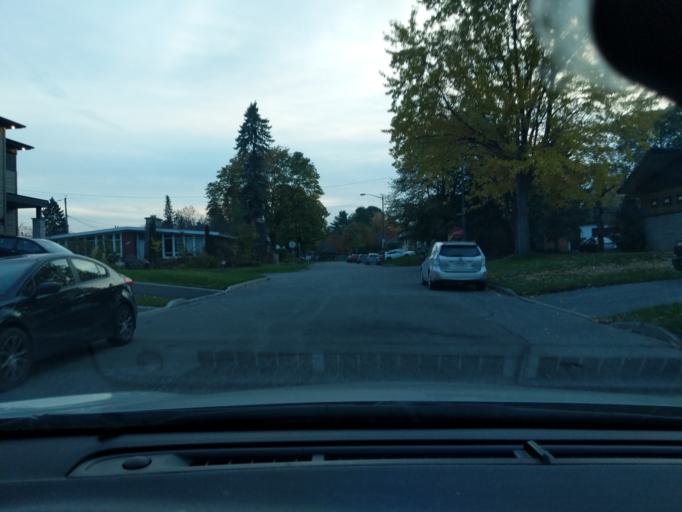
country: CA
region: Quebec
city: Quebec
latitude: 46.7623
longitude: -71.2759
